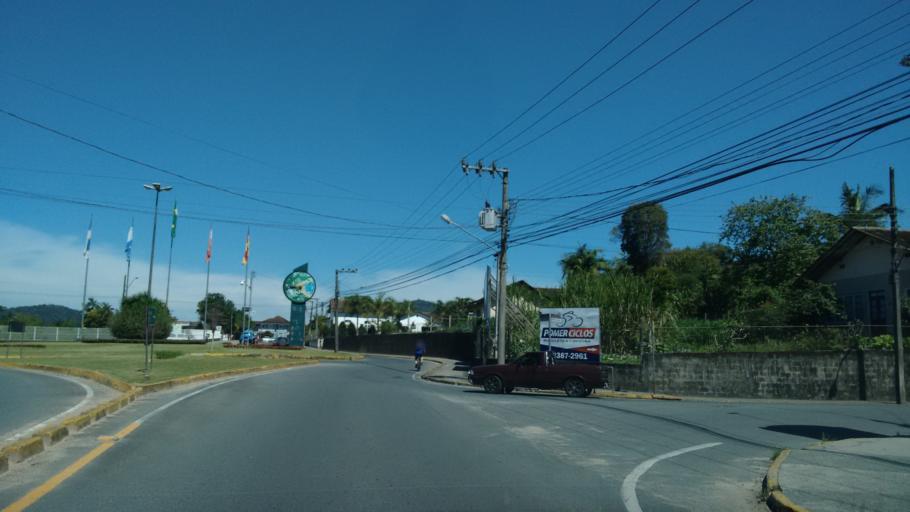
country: BR
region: Santa Catarina
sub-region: Pomerode
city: Pomerode
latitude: -26.7505
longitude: -49.1736
